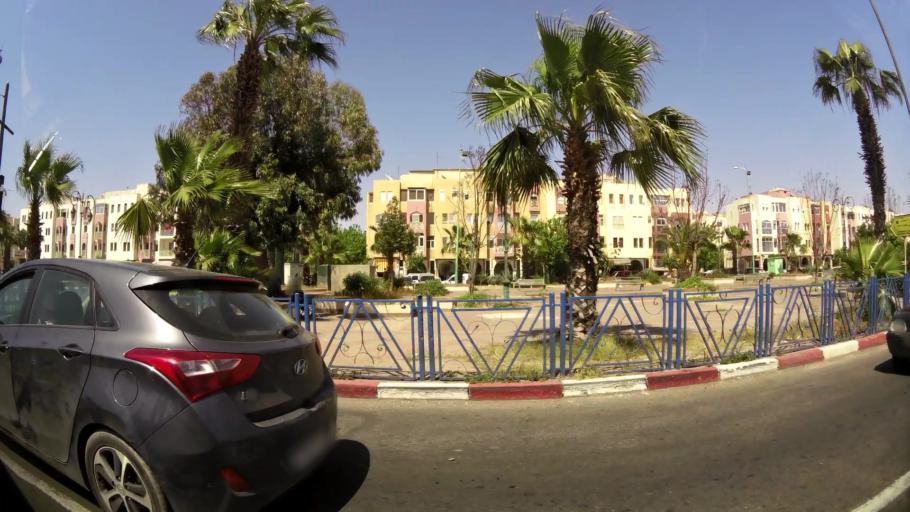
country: MA
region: Souss-Massa-Draa
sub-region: Inezgane-Ait Mellou
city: Inezgane
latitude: 30.3607
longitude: -9.5272
